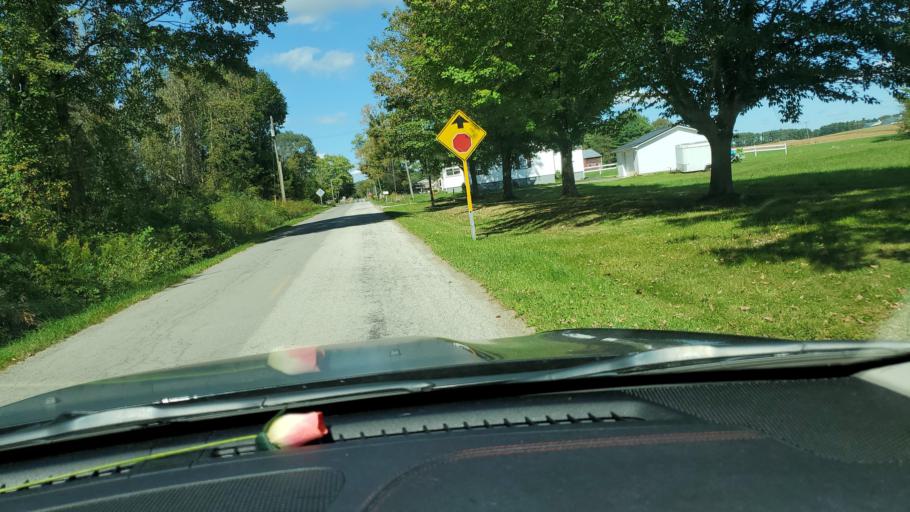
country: US
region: Ohio
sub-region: Ashtabula County
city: Andover
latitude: 41.4532
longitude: -80.5862
